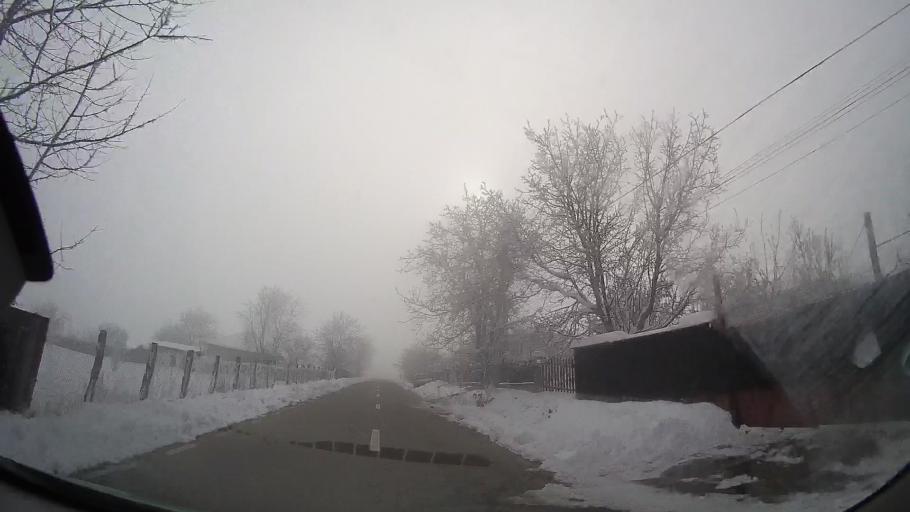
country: RO
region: Iasi
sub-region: Comuna Valea Seaca
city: Valea Seaca
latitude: 47.2828
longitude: 26.6696
